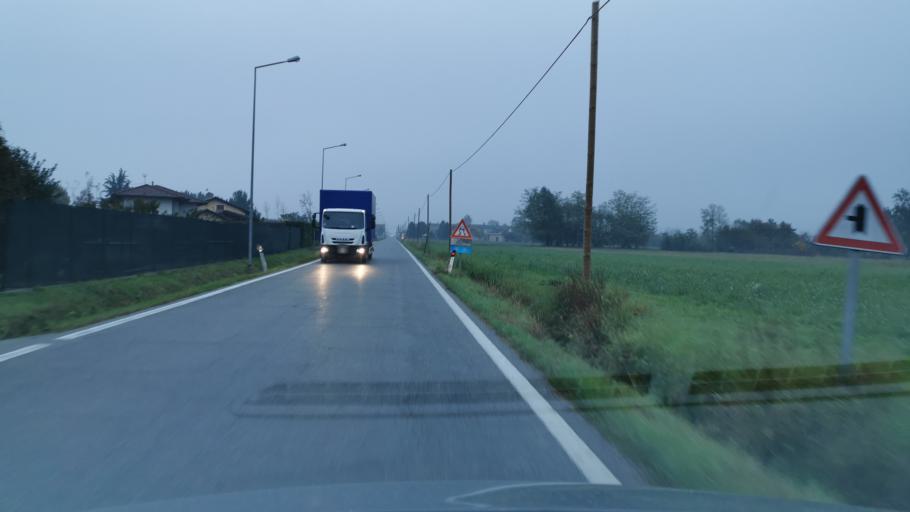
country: IT
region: Piedmont
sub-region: Provincia di Torino
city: Ciconio
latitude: 45.3309
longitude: 7.7622
